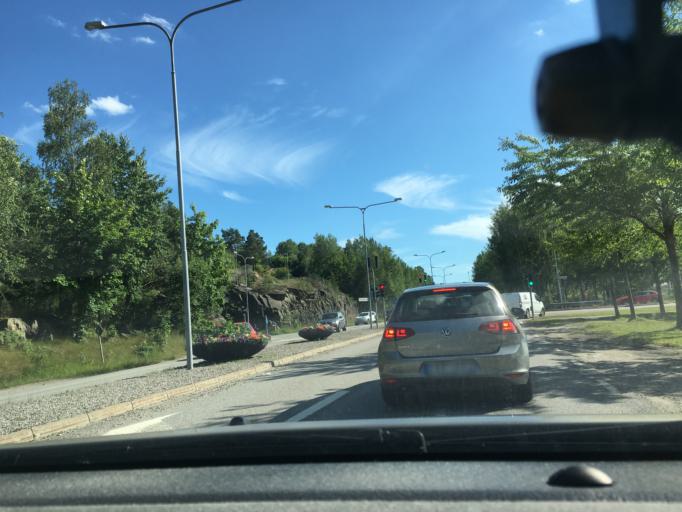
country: SE
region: Stockholm
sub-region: Nacka Kommun
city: Boo
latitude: 59.3271
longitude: 18.2610
